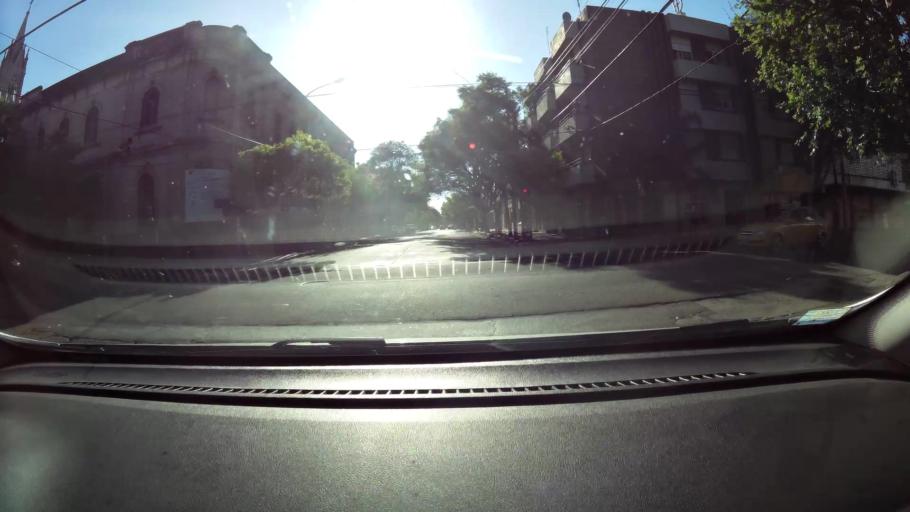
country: AR
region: Cordoba
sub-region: Departamento de Capital
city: Cordoba
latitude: -31.3875
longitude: -64.1838
